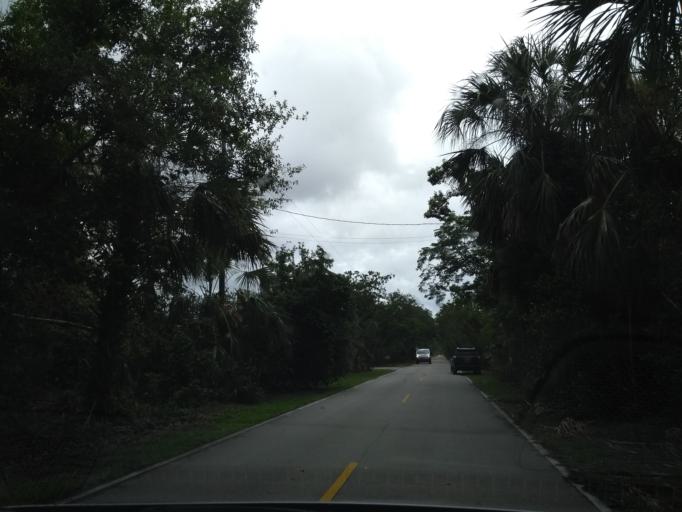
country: US
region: Florida
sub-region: Miami-Dade County
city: The Hammocks
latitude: 25.7464
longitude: -80.9473
